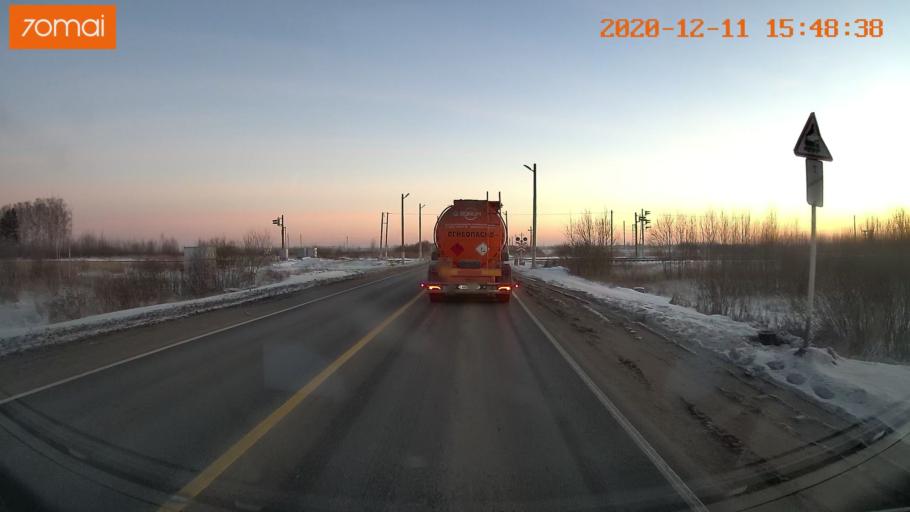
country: RU
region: Ivanovo
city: Novo-Talitsy
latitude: 56.9919
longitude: 40.8696
